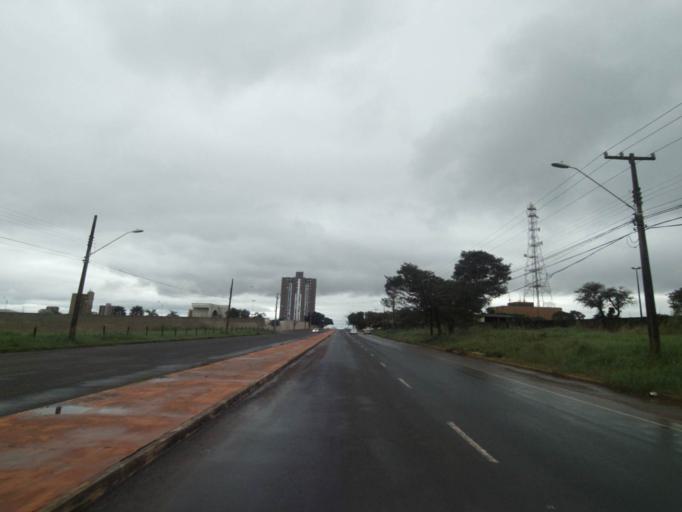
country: BR
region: Parana
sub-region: Foz Do Iguacu
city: Foz do Iguacu
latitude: -25.5180
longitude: -54.5675
